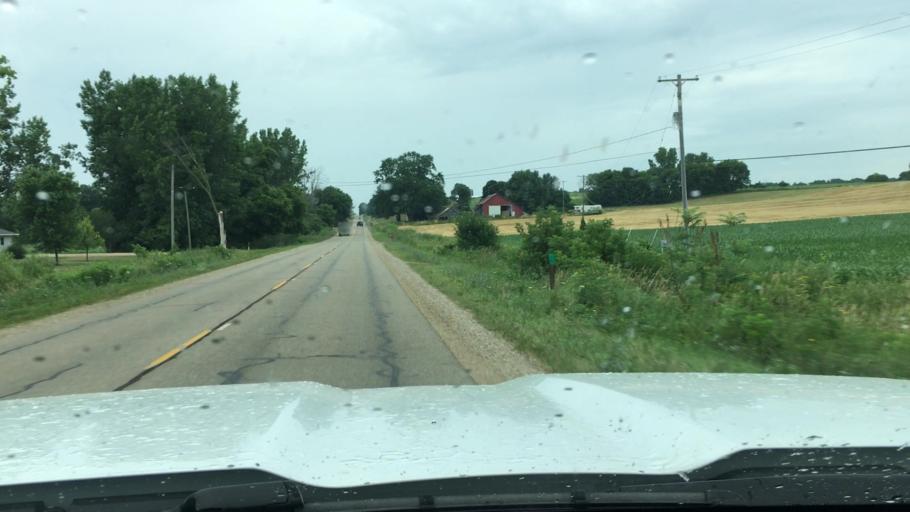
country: US
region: Michigan
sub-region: Ottawa County
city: Hudsonville
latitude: 42.7896
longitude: -85.8417
